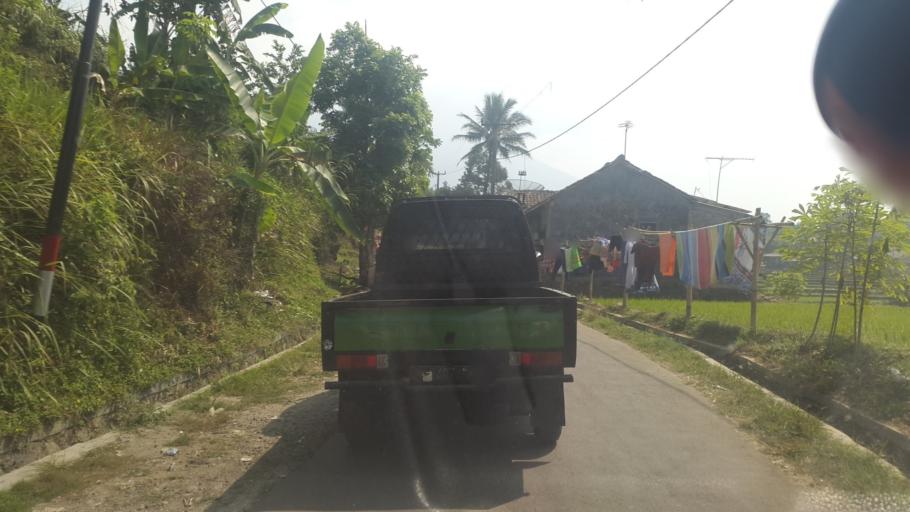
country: ID
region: West Java
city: Cicurug
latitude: -6.7740
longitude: 106.7467
